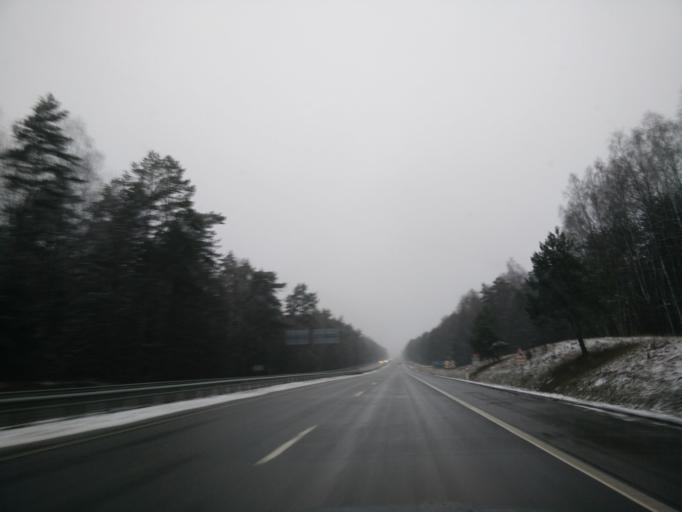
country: LT
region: Vilnius County
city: Lazdynai
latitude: 54.6427
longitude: 25.1793
